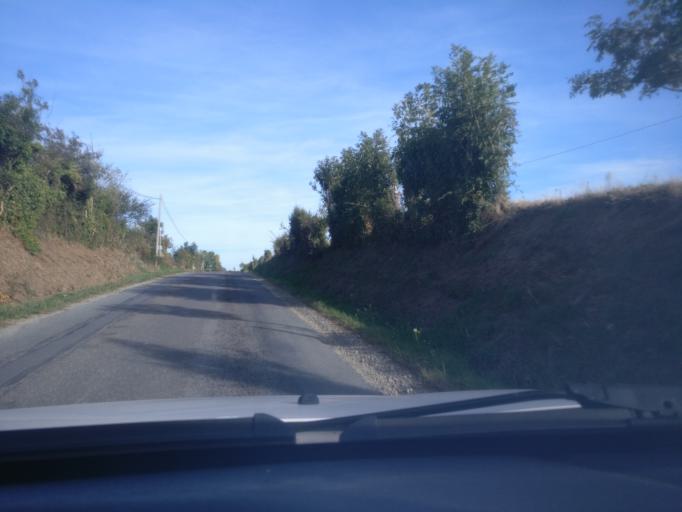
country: FR
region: Lower Normandy
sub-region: Departement de la Manche
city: Sartilly
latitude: 48.7085
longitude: -1.4814
